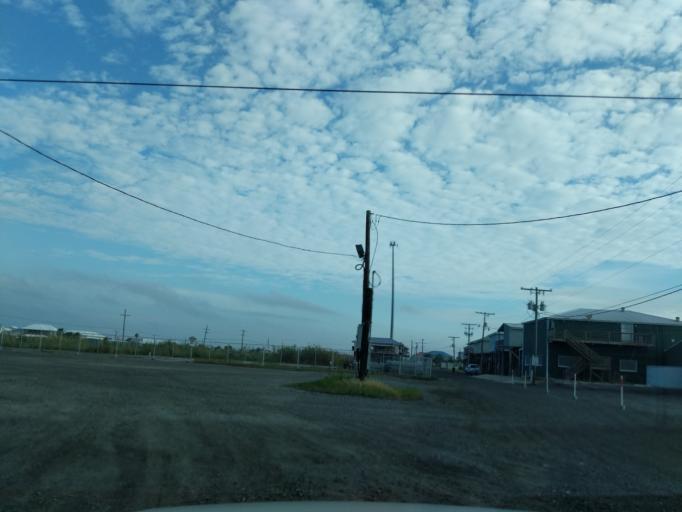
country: US
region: Louisiana
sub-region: Terrebonne Parish
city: Dulac
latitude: 29.2466
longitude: -90.6615
